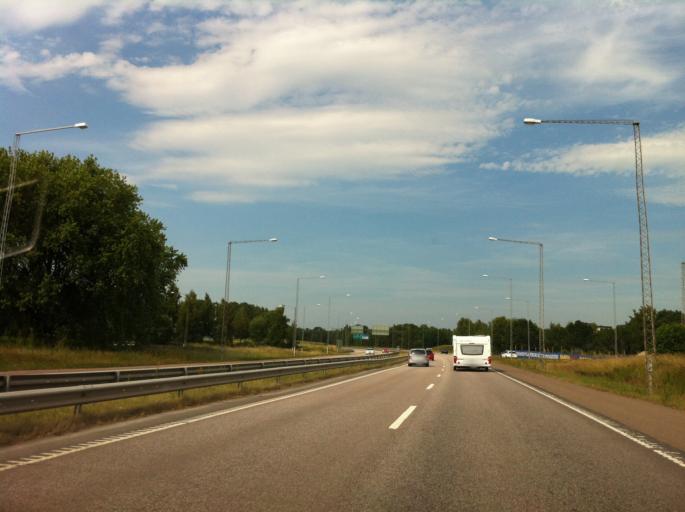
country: SE
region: Kalmar
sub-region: Kalmar Kommun
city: Rinkabyholm
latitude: 56.6690
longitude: 16.3060
